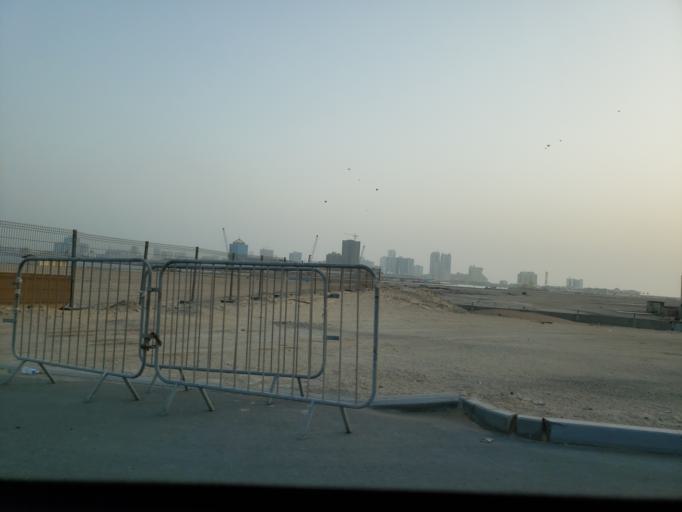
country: AE
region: Ajman
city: Ajman
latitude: 25.4288
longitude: 55.4609
